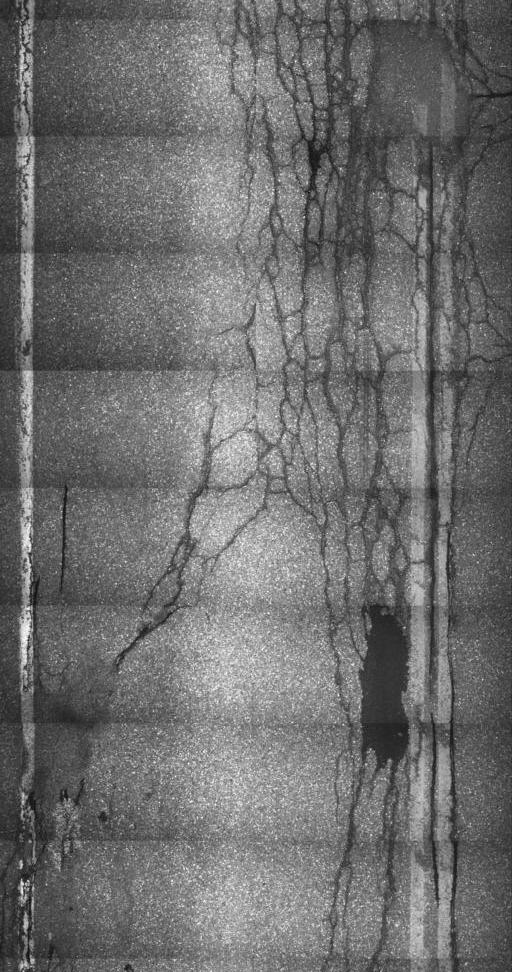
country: US
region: Vermont
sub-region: Addison County
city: Bristol
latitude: 44.1315
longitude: -73.0472
